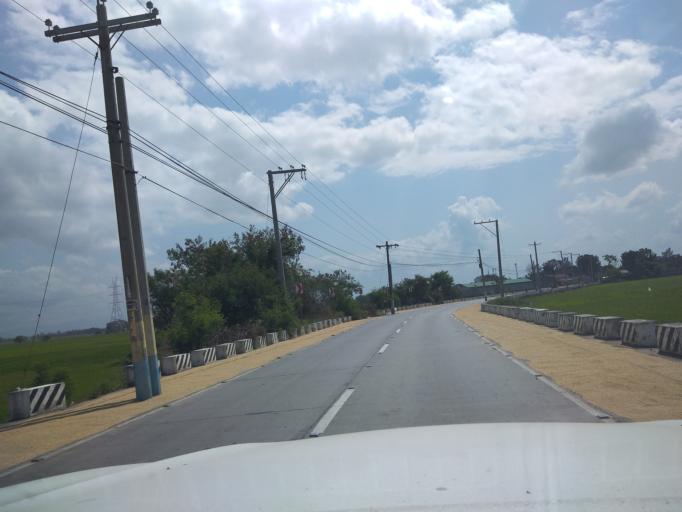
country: PH
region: Central Luzon
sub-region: Province of Pampanga
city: Talang
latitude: 15.0235
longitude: 120.8449
